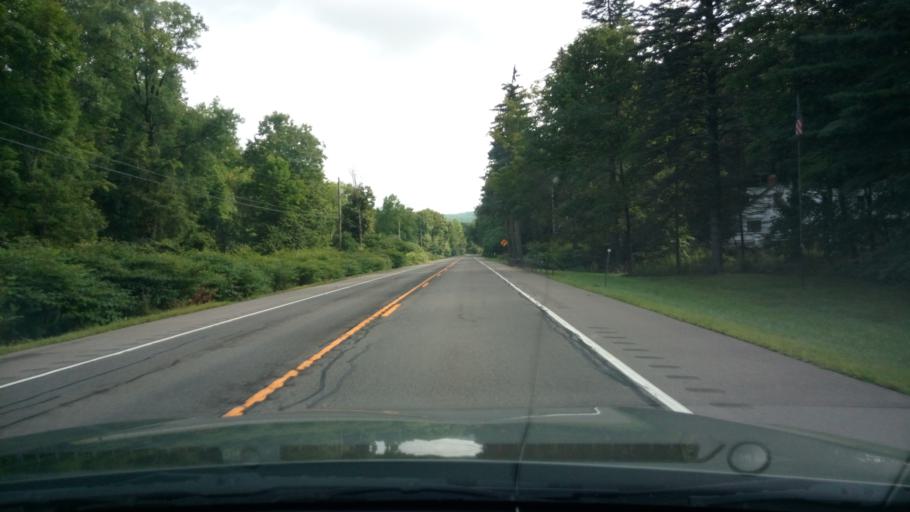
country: US
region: New York
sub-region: Chemung County
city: Horseheads North
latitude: 42.2884
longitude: -76.7317
